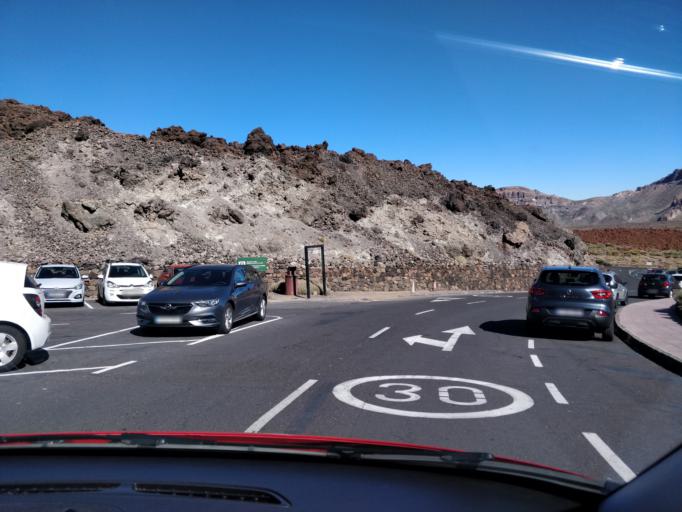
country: ES
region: Canary Islands
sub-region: Provincia de Santa Cruz de Tenerife
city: Vilaflor
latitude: 28.2562
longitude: -16.6232
